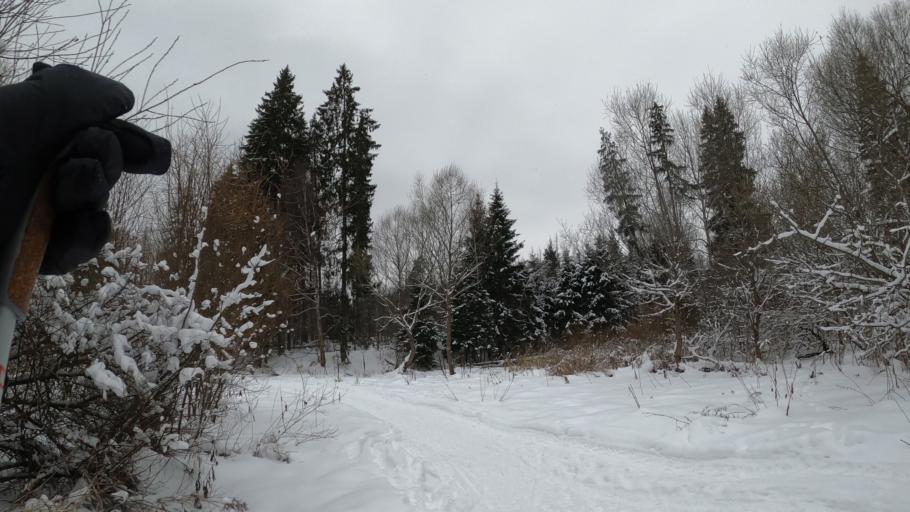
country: RU
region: Moskovskaya
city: Firsanovka
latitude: 55.9406
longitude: 37.2212
